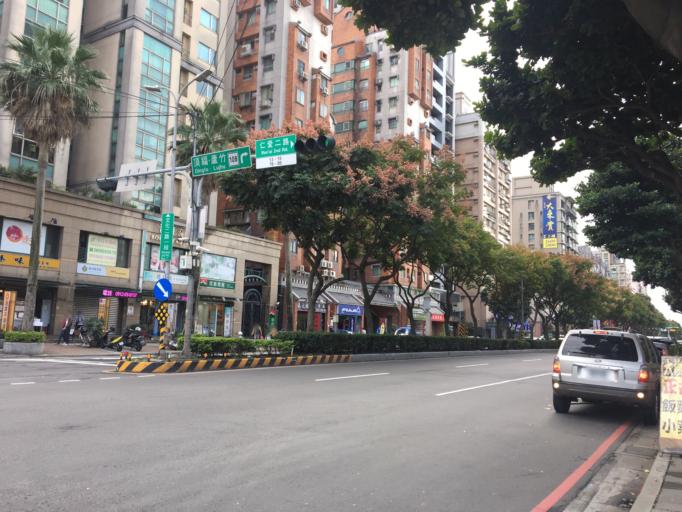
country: TW
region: Taiwan
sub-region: Taoyuan
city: Taoyuan
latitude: 25.0735
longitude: 121.3706
